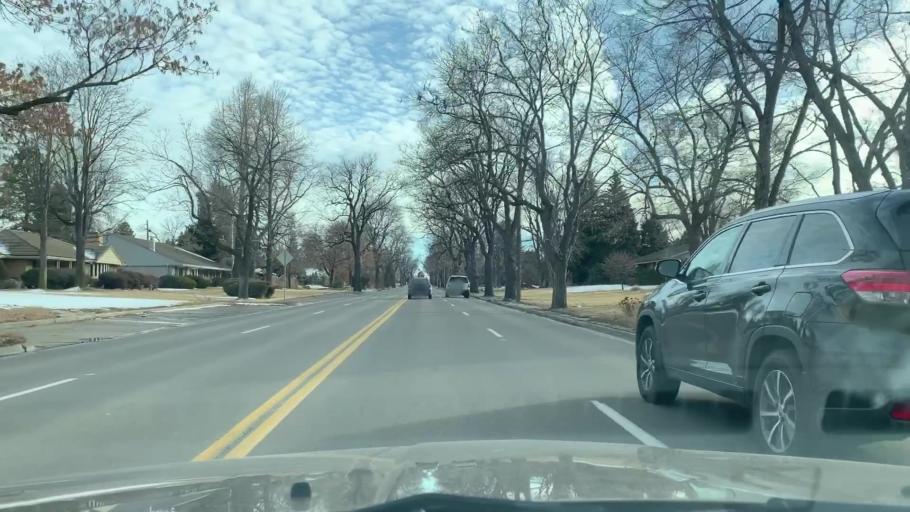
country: US
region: Colorado
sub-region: Arapahoe County
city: Glendale
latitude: 39.7246
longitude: -104.9128
